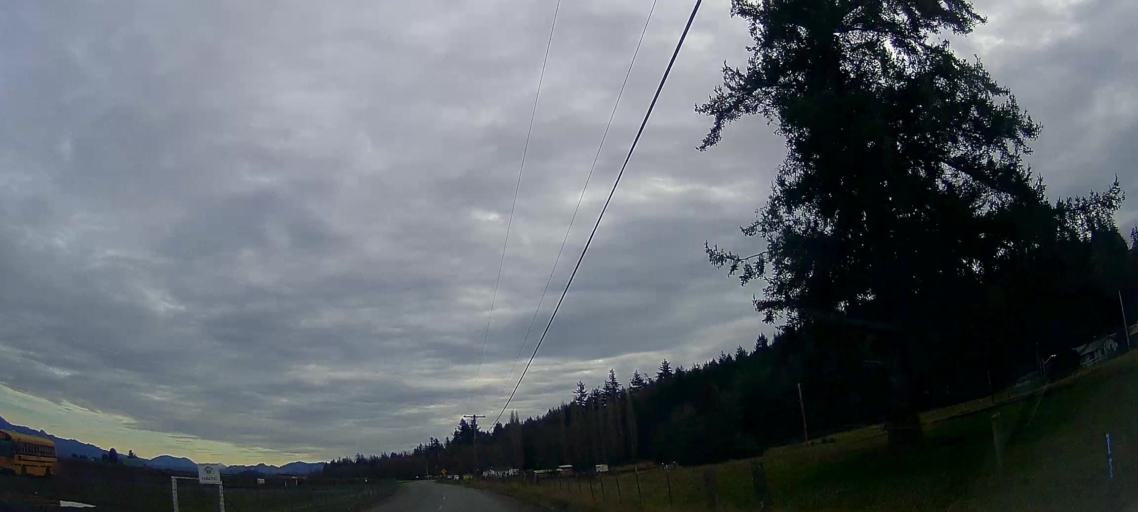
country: US
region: Washington
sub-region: Skagit County
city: Burlington
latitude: 48.5058
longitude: -122.4229
